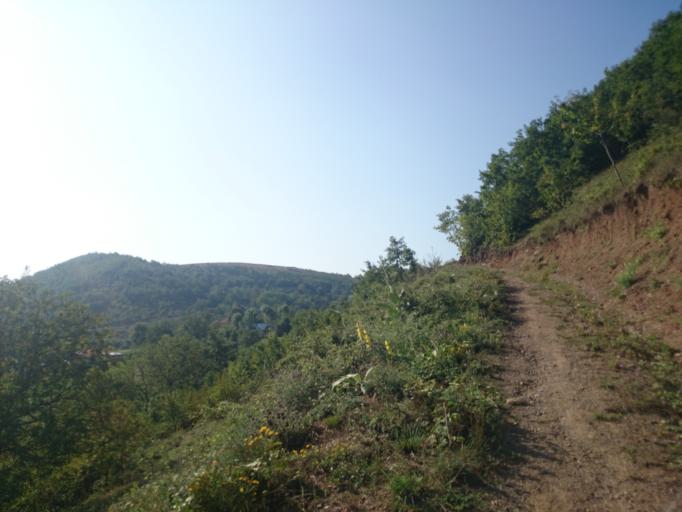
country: AL
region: Diber
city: Peshkopi
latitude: 41.6410
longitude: 20.4013
